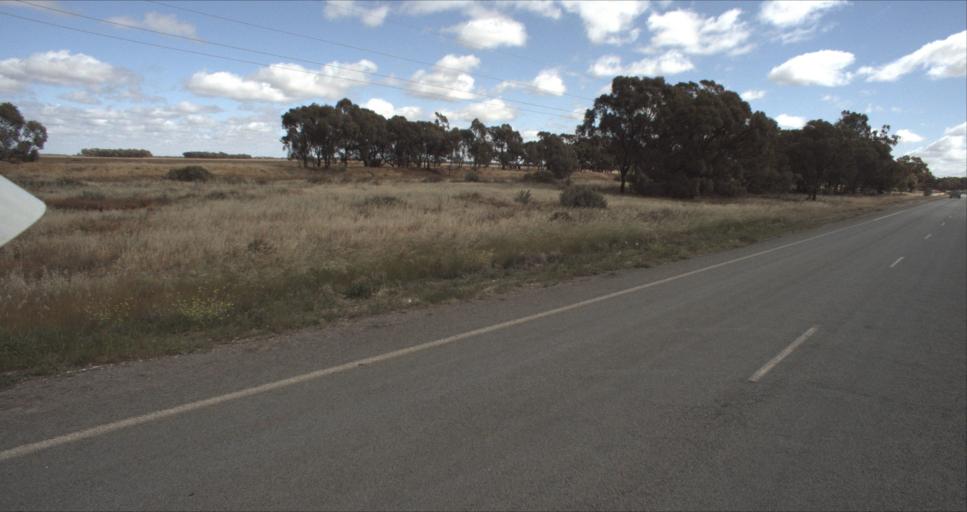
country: AU
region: New South Wales
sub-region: Murrumbidgee Shire
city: Darlington Point
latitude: -34.5736
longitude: 146.1667
